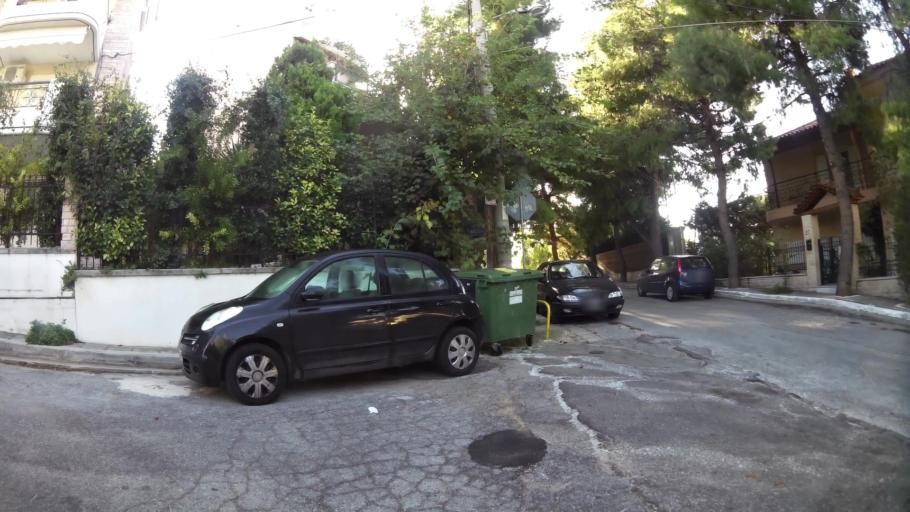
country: GR
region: Attica
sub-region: Nomarchia Athinas
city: Lykovrysi
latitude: 38.0575
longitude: 23.7798
